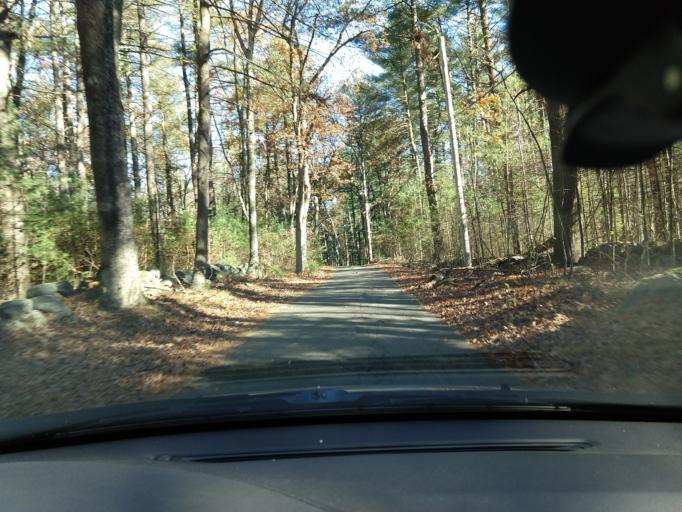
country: US
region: Massachusetts
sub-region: Middlesex County
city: Concord
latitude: 42.4891
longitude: -71.3300
